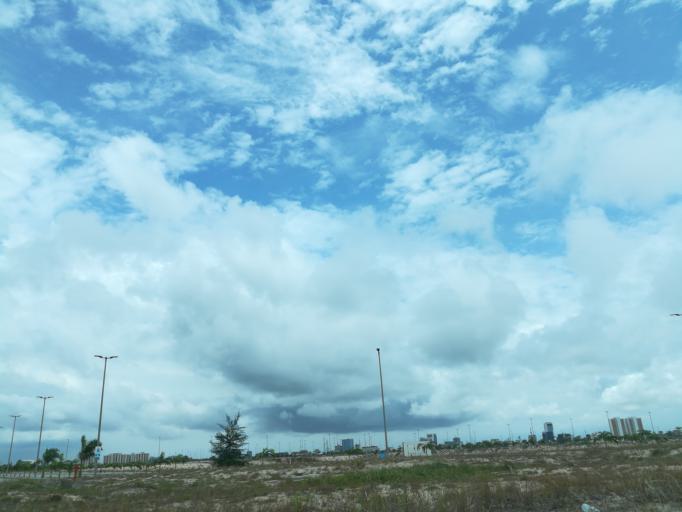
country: NG
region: Lagos
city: Ikoyi
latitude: 6.4082
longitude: 3.4158
